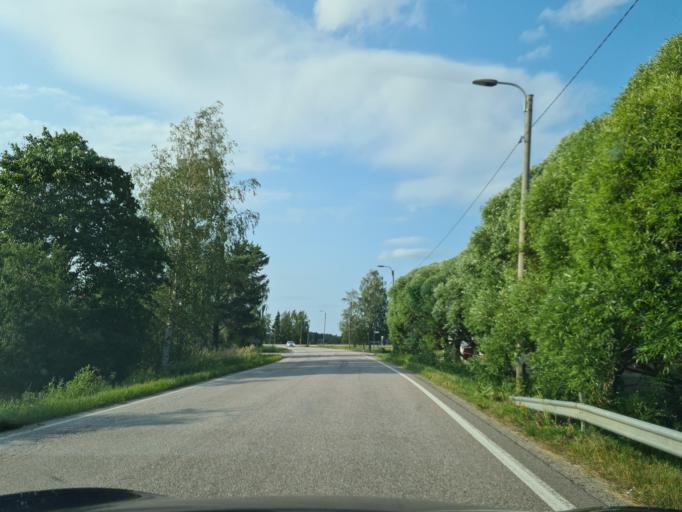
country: FI
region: Ostrobothnia
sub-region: Vaasa
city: Vaehaekyroe
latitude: 63.0094
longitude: 22.1491
